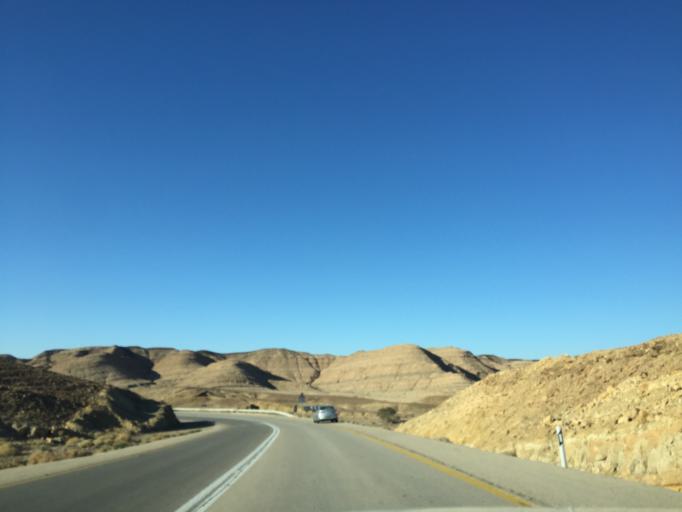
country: IL
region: Southern District
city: Mitzpe Ramon
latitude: 30.5930
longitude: 34.8895
